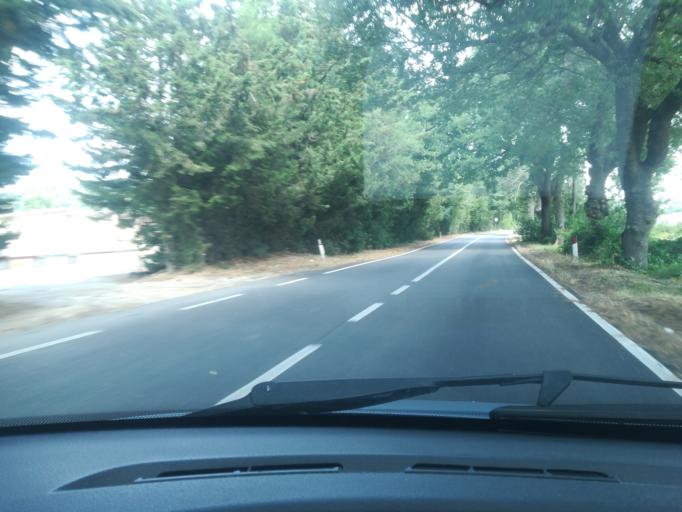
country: IT
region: The Marches
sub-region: Provincia di Macerata
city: Sforzacosta
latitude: 43.2716
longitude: 13.4364
